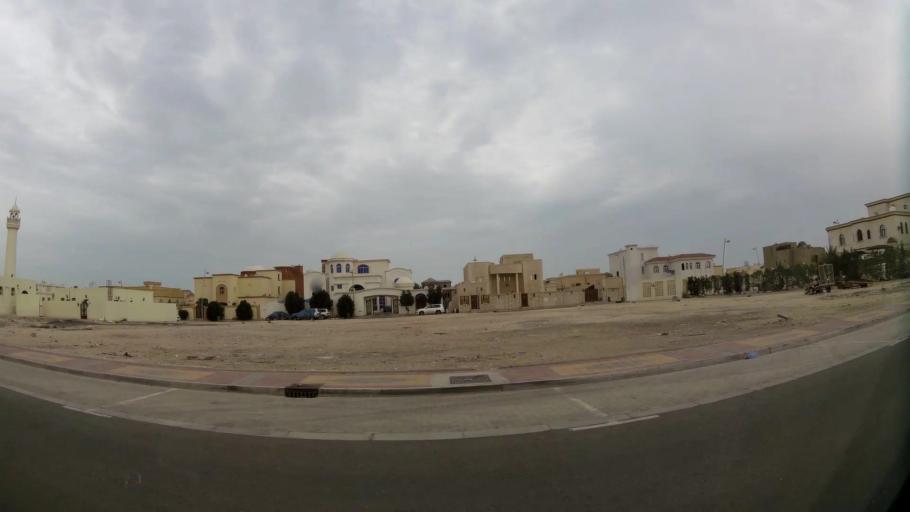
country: QA
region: Baladiyat ad Dawhah
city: Doha
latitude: 25.3430
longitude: 51.4834
